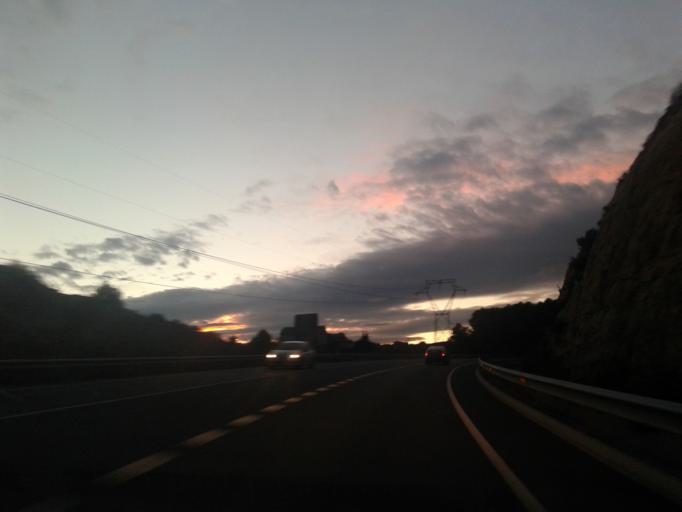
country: ES
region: Catalonia
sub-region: Provincia de Barcelona
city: Olesa de Bonesvalls
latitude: 41.3884
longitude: 1.8780
